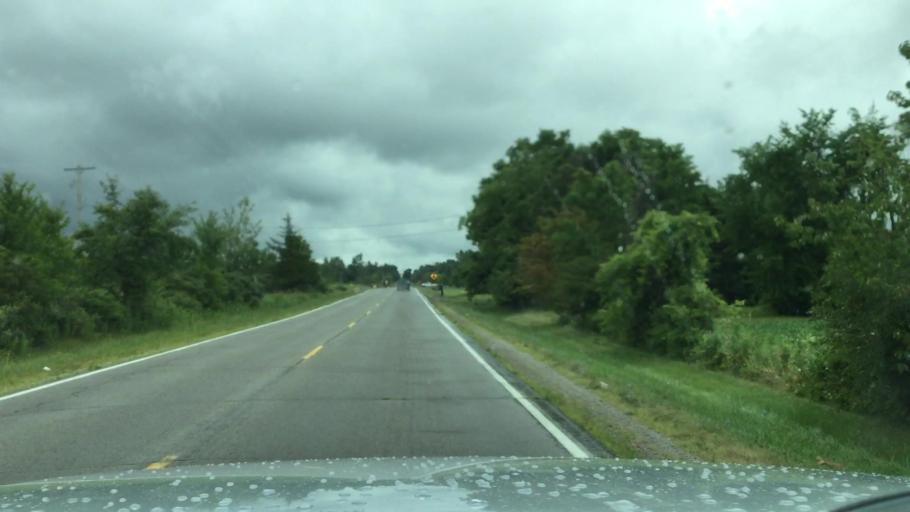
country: US
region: Michigan
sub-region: Genesee County
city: Clio
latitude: 43.1222
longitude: -83.7738
